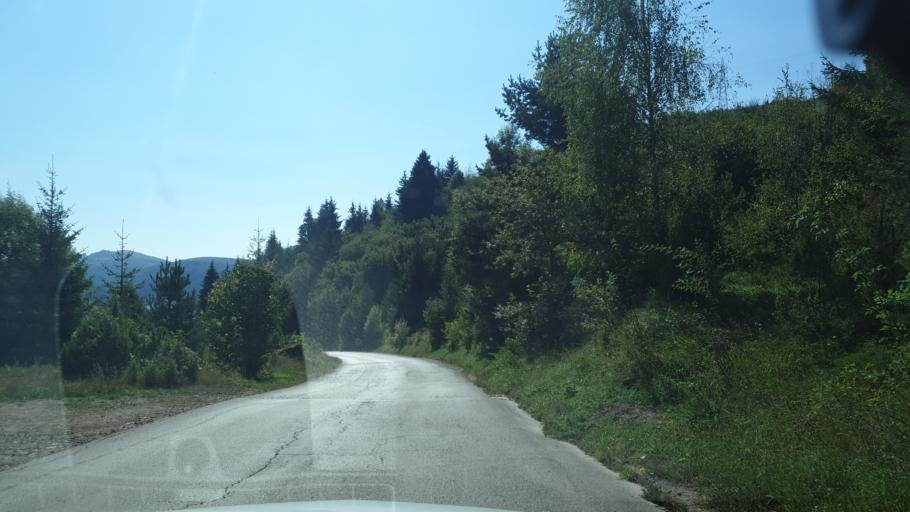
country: RS
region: Central Serbia
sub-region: Zlatiborski Okrug
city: Nova Varos
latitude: 43.4239
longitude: 19.9212
